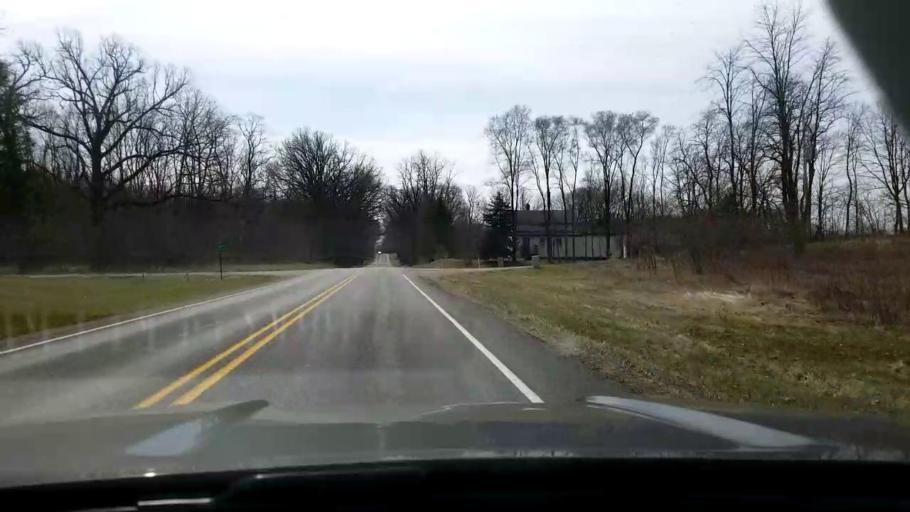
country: US
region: Michigan
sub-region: Jackson County
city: Spring Arbor
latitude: 42.1797
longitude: -84.5203
